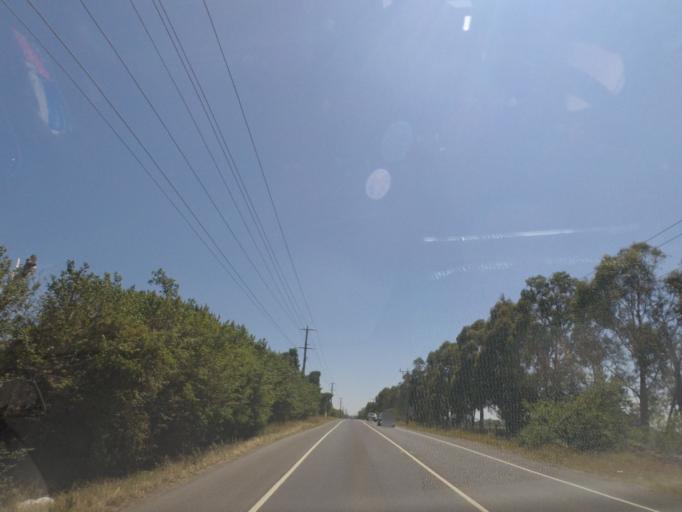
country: AU
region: Victoria
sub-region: Whittlesea
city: Epping
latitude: -37.6044
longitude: 145.0320
